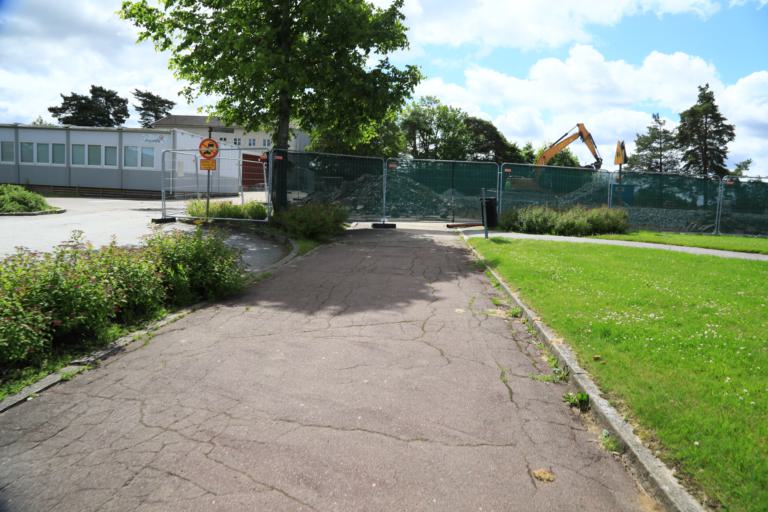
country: SE
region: Vaestra Goetaland
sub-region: Marks Kommun
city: Kinna
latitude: 57.5054
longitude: 12.6920
